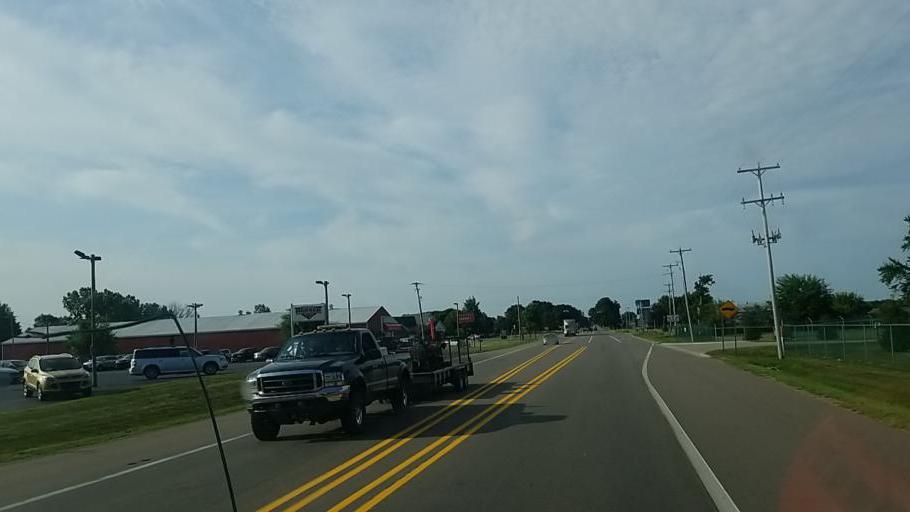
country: US
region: Michigan
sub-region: Ionia County
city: Ionia
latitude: 42.9312
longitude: -85.0749
